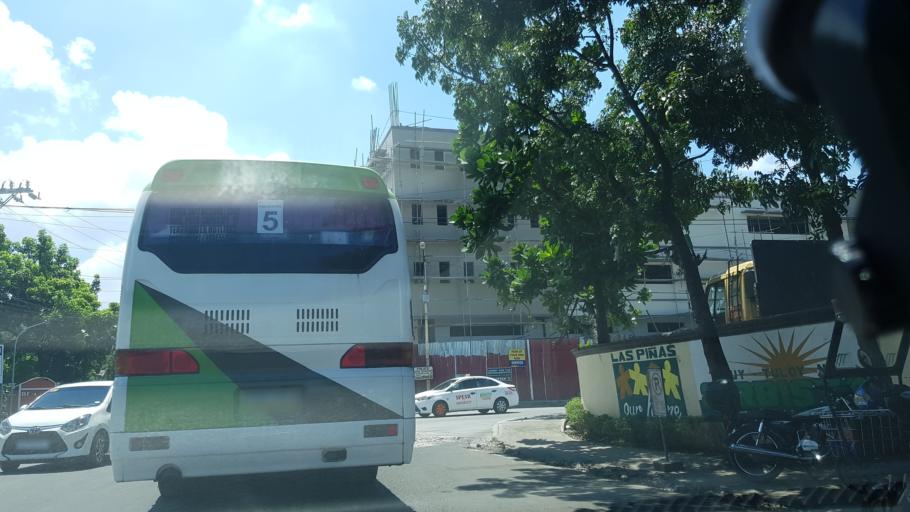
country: PH
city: Sambayanihan People's Village
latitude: 14.4713
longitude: 120.9986
